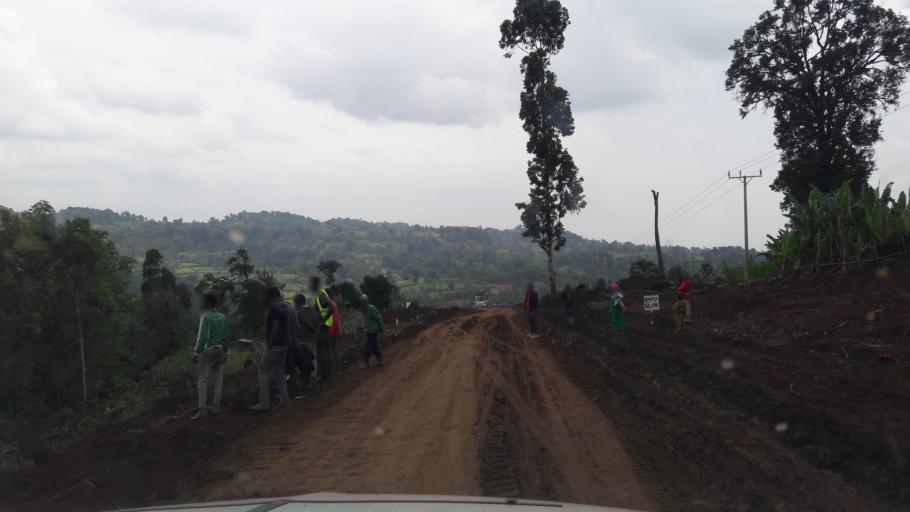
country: ET
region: Southern Nations, Nationalities, and People's Region
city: Tippi
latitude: 7.6497
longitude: 35.5061
